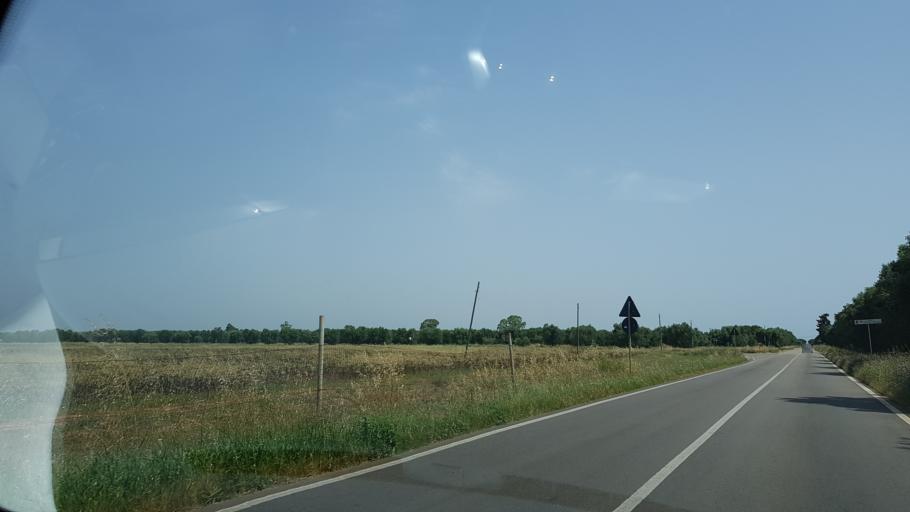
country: IT
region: Apulia
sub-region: Provincia di Brindisi
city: San Pancrazio Salentino
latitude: 40.3559
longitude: 17.8441
